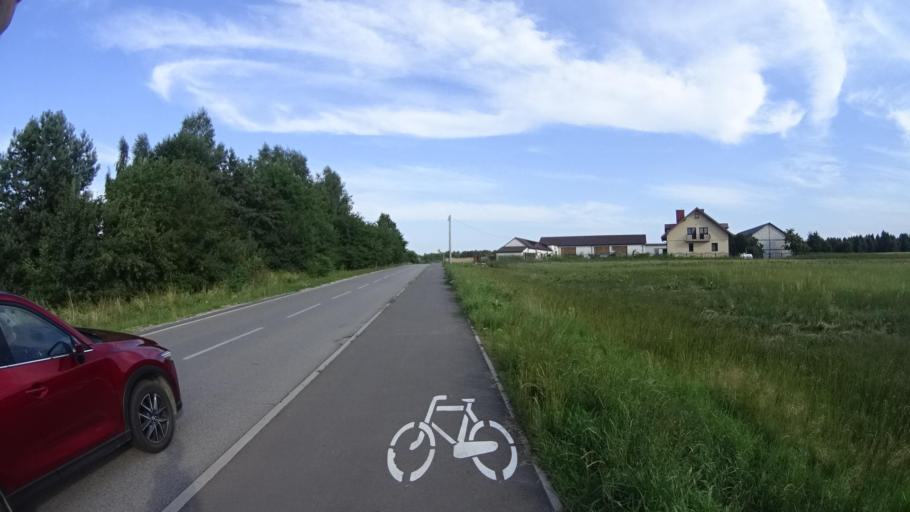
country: PL
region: Masovian Voivodeship
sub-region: Powiat piaseczynski
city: Tarczyn
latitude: 52.0160
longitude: 20.7960
